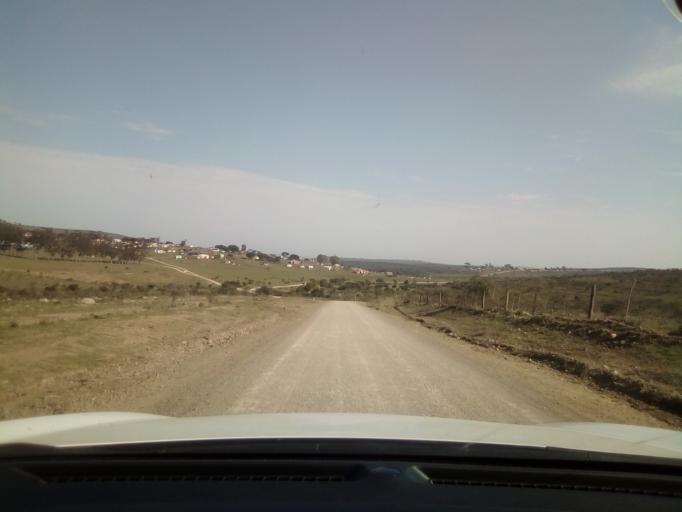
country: ZA
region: Eastern Cape
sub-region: Buffalo City Metropolitan Municipality
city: Bhisho
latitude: -32.9881
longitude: 27.2436
